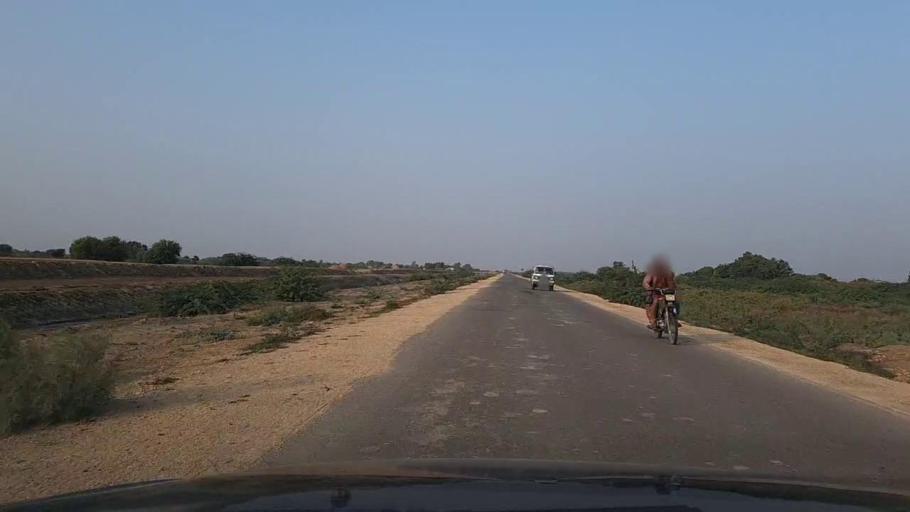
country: PK
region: Sindh
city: Mirpur Sakro
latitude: 24.4800
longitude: 67.8045
